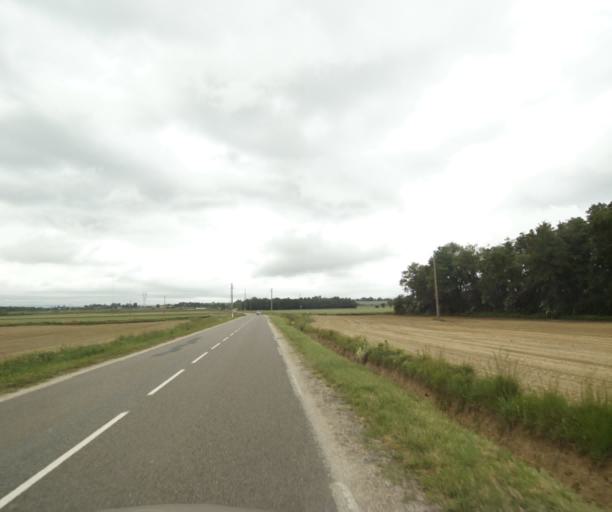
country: FR
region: Rhone-Alpes
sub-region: Departement de l'Ain
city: Saint-Maurice-de-Beynost
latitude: 45.8514
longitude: 4.9585
